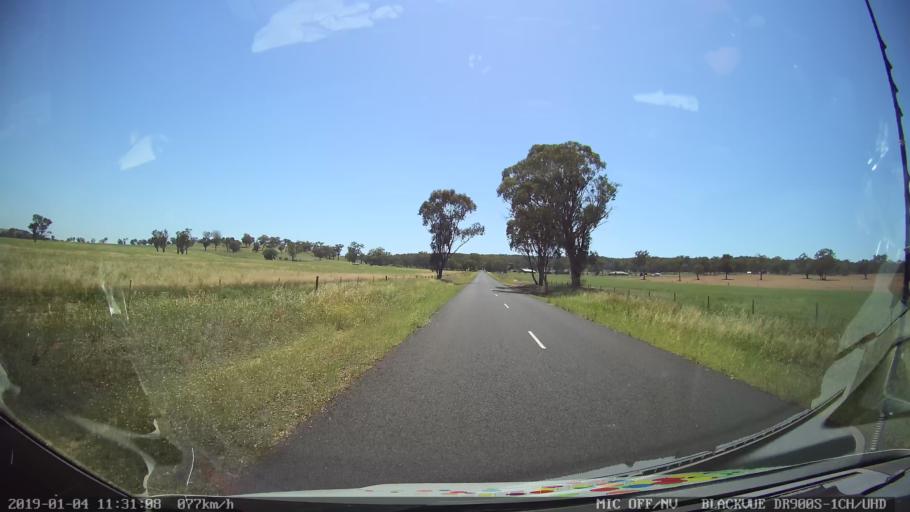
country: AU
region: New South Wales
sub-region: Cabonne
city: Molong
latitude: -33.0737
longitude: 148.7896
